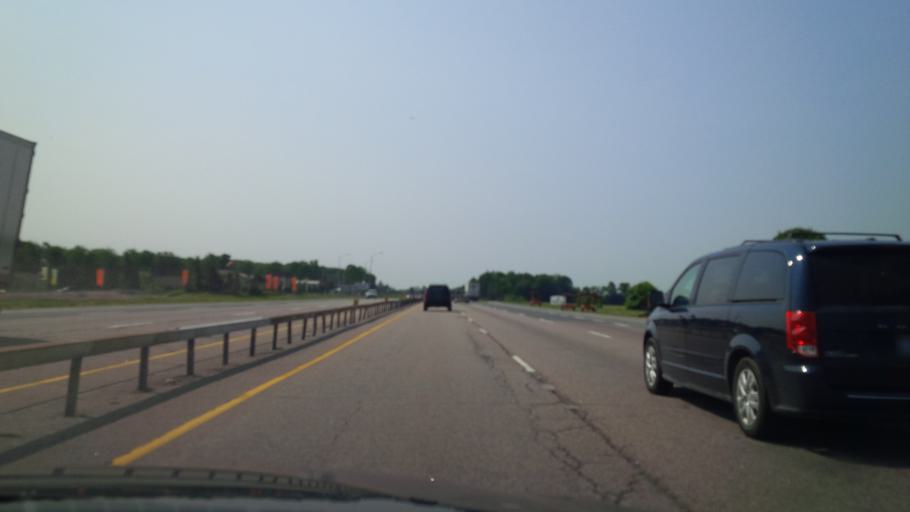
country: CA
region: Ontario
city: Innisfil
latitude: 44.2843
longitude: -79.6795
